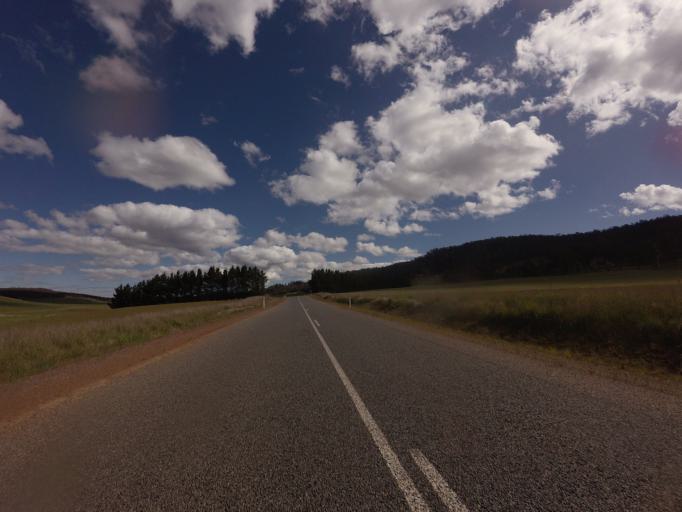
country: AU
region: Tasmania
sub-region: Brighton
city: Bridgewater
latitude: -42.4371
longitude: 147.3123
